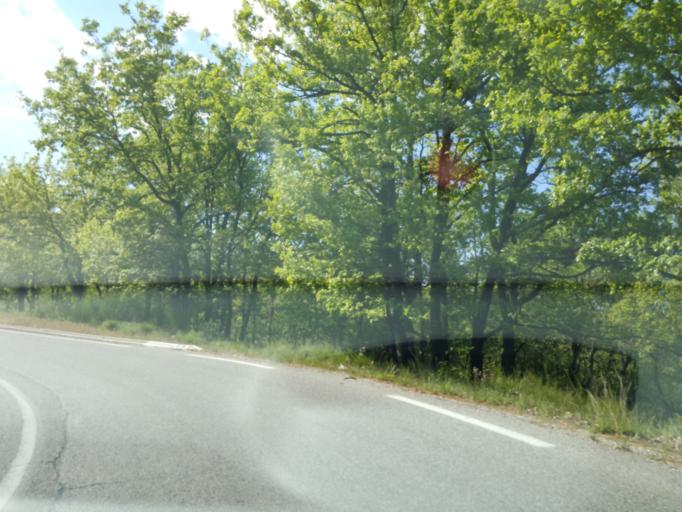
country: FR
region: Provence-Alpes-Cote d'Azur
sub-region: Departement du Var
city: La Roquebrussanne
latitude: 43.3724
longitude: 5.9724
